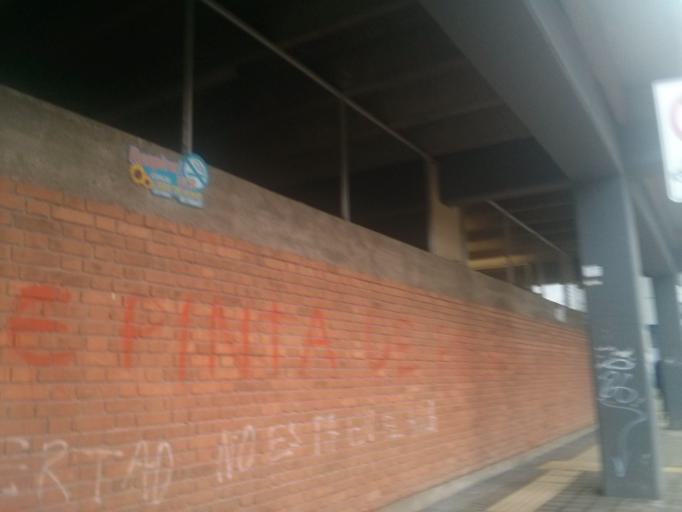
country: CR
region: San Jose
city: San Pedro
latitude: 9.9346
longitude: -84.0527
